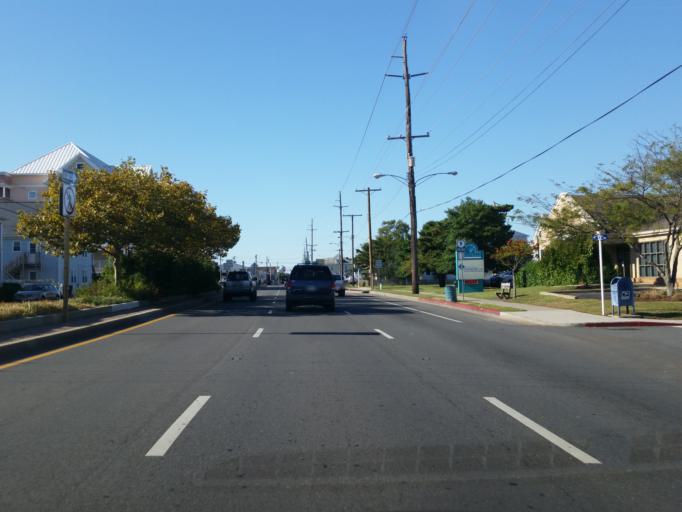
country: US
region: Maryland
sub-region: Worcester County
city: Ocean City
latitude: 38.3420
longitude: -75.0820
